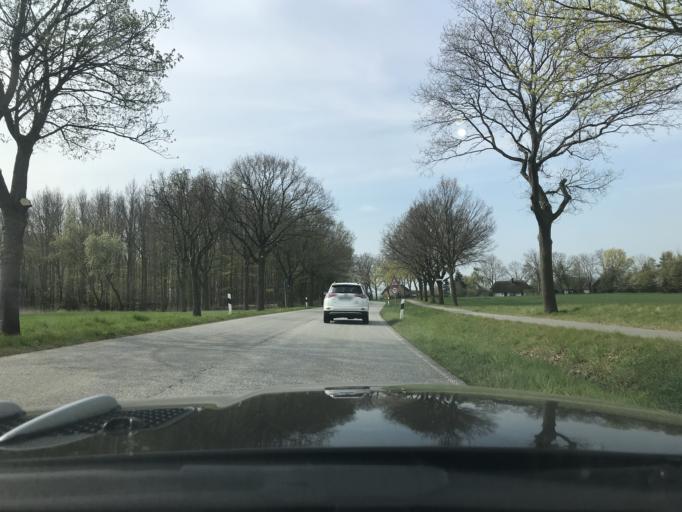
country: DE
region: Schleswig-Holstein
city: Grube
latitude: 54.2554
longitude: 11.0332
